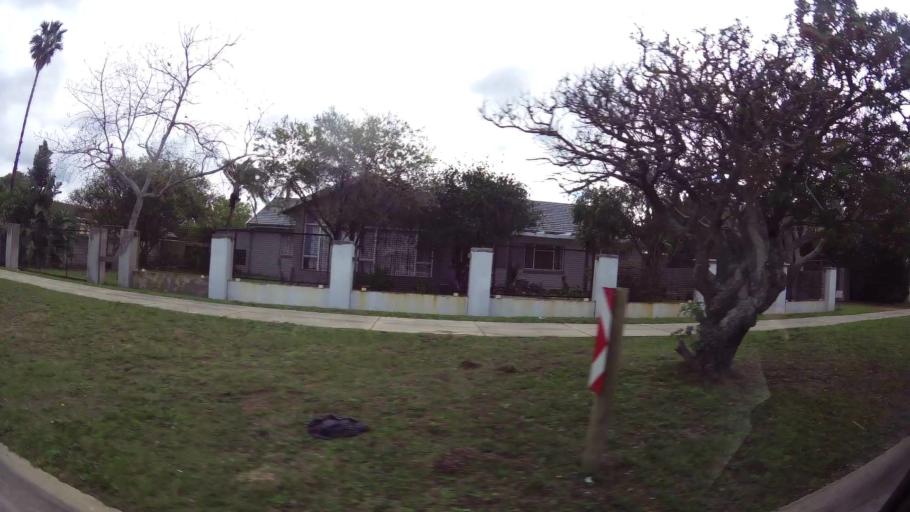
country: ZA
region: Eastern Cape
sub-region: Nelson Mandela Bay Metropolitan Municipality
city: Port Elizabeth
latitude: -33.9372
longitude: 25.5232
